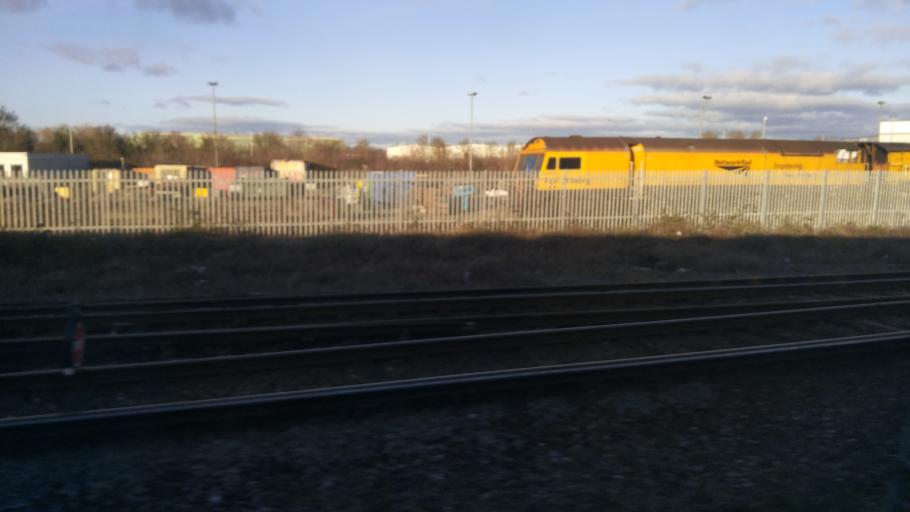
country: GB
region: England
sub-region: Kent
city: Paddock Wood
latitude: 51.1823
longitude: 0.3928
